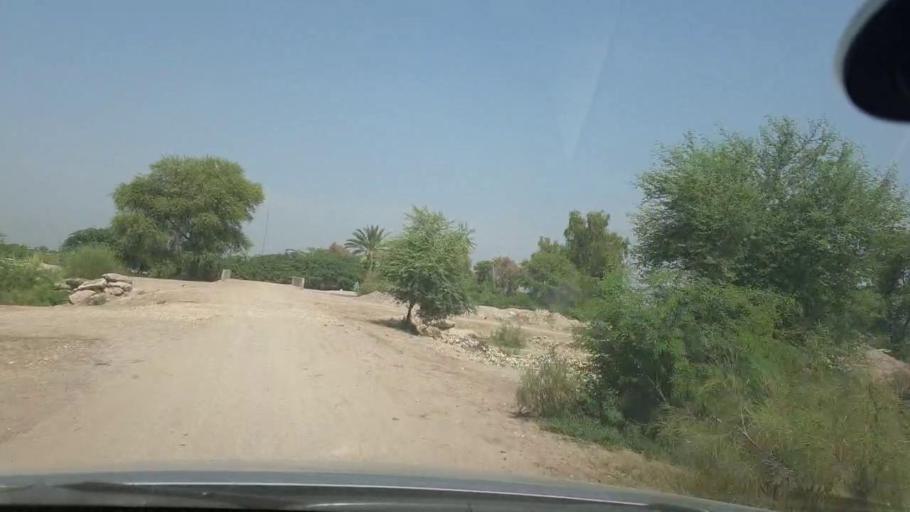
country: PK
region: Balochistan
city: Mehrabpur
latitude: 28.0906
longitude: 68.0390
